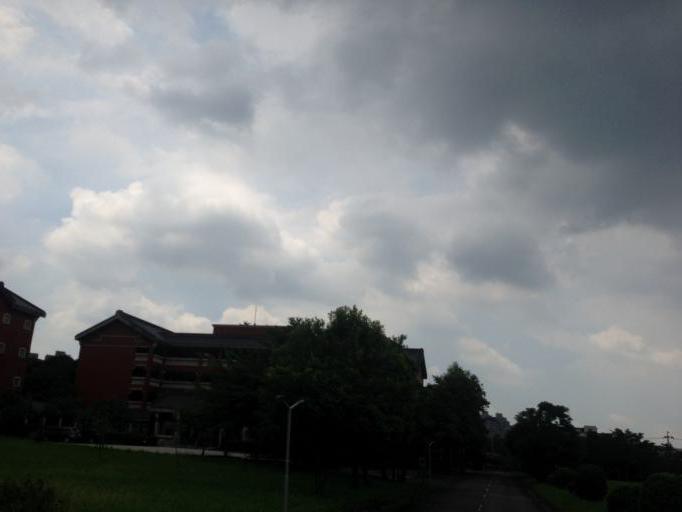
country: TW
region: Taiwan
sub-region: Taoyuan
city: Taoyuan
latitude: 24.9369
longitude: 121.3819
